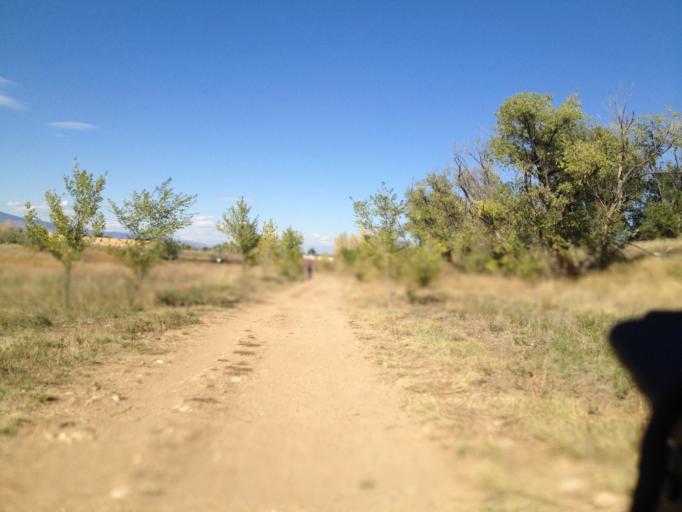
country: US
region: Colorado
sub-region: Boulder County
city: Boulder
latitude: 39.9792
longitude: -105.2293
